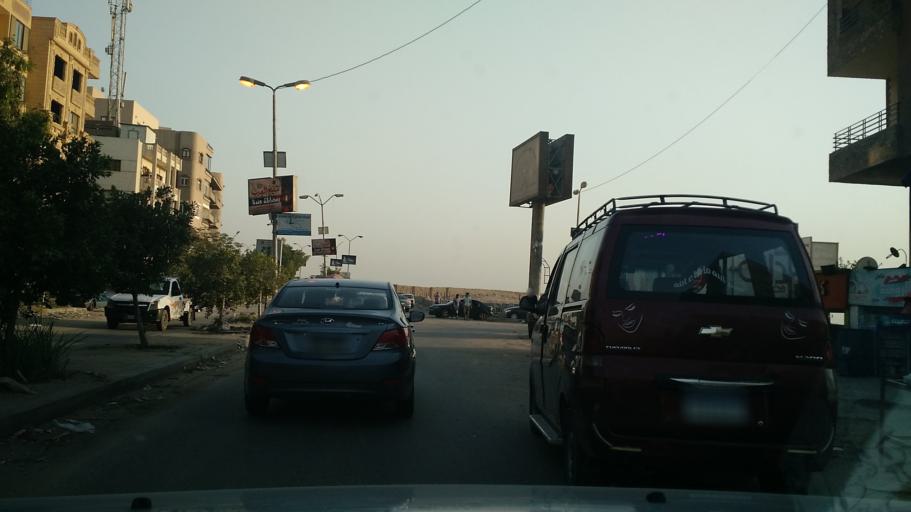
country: EG
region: Muhafazat al Qahirah
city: Cairo
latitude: 30.0021
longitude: 31.2891
